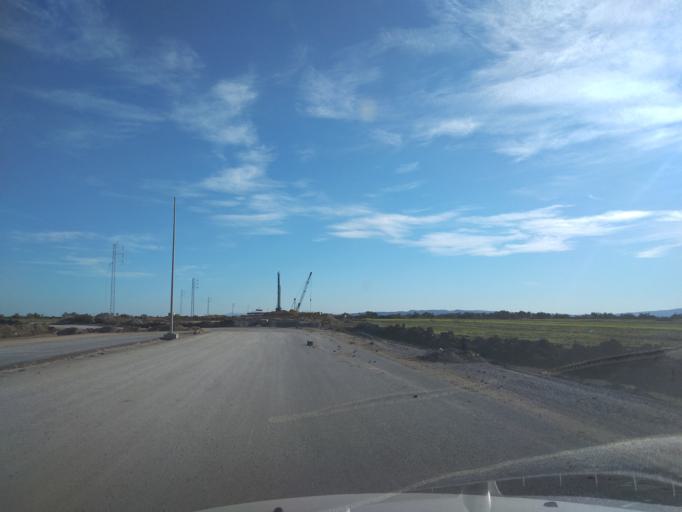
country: TN
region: Ariana
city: Qal'at al Andalus
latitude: 37.0262
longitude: 10.1389
